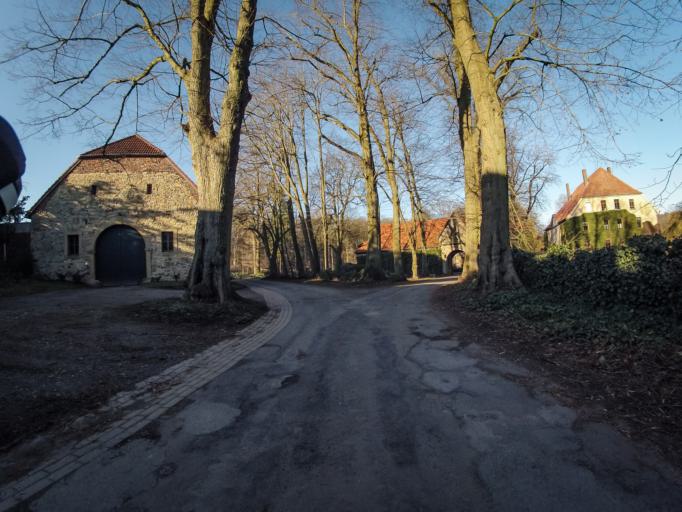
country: DE
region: Lower Saxony
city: Osnabrueck
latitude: 52.3088
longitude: 8.0305
